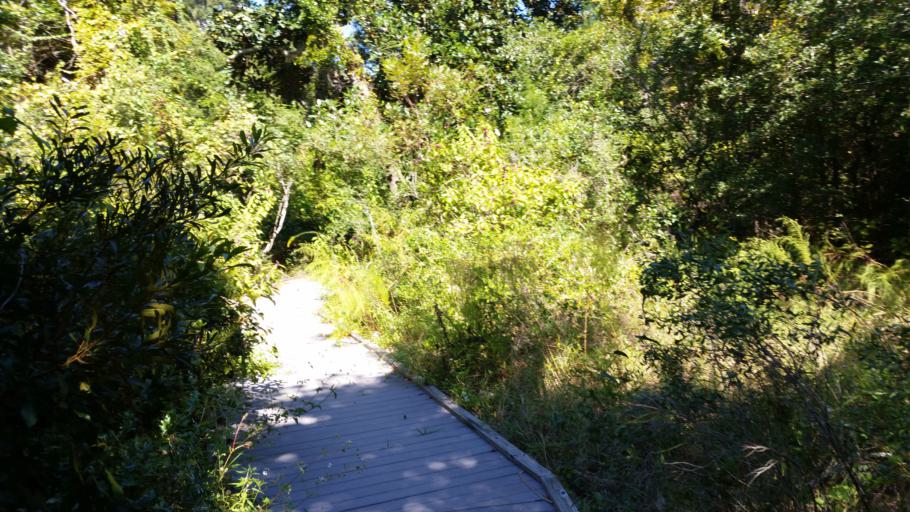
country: US
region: Florida
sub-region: Santa Rosa County
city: Gulf Breeze
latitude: 30.3634
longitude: -87.1326
